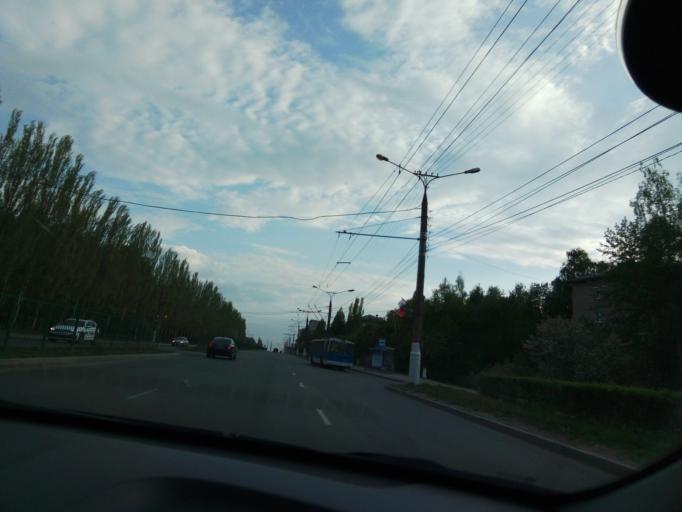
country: RU
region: Chuvashia
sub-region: Cheboksarskiy Rayon
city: Cheboksary
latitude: 56.1289
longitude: 47.2870
